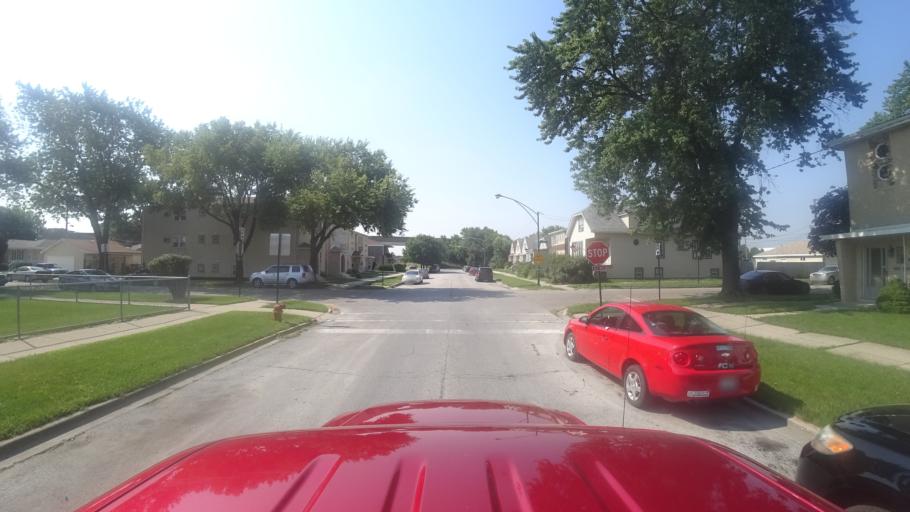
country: US
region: Illinois
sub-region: Cook County
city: Cicero
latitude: 41.7970
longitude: -87.7356
